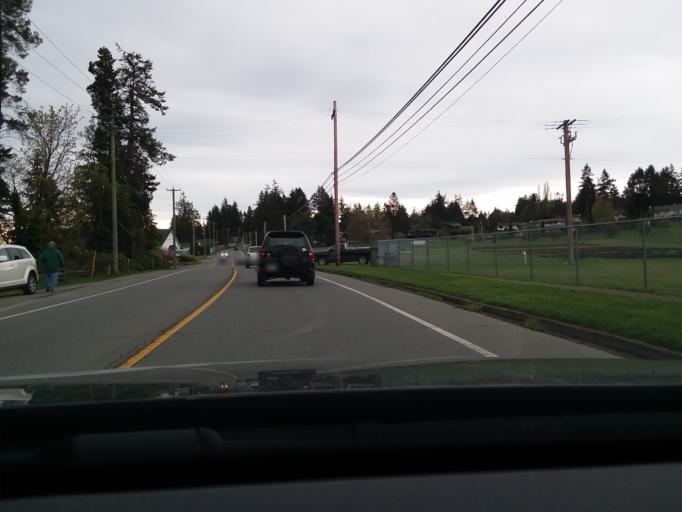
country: CA
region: British Columbia
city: North Saanich
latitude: 48.6219
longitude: -123.4181
